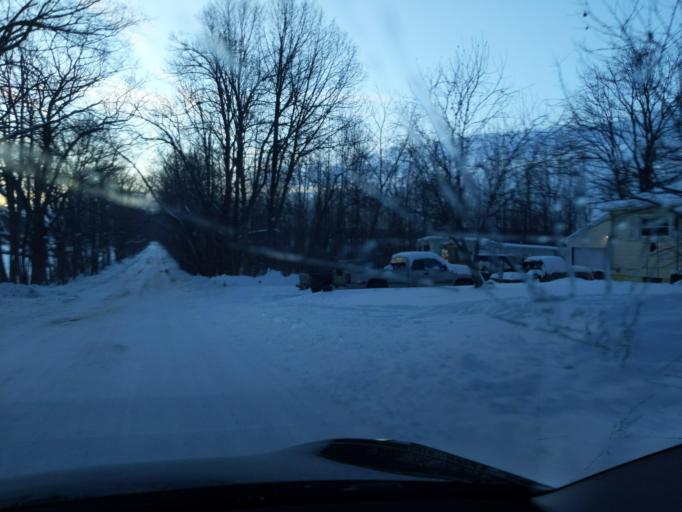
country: US
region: Michigan
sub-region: Ingham County
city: Mason
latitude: 42.5703
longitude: -84.3481
